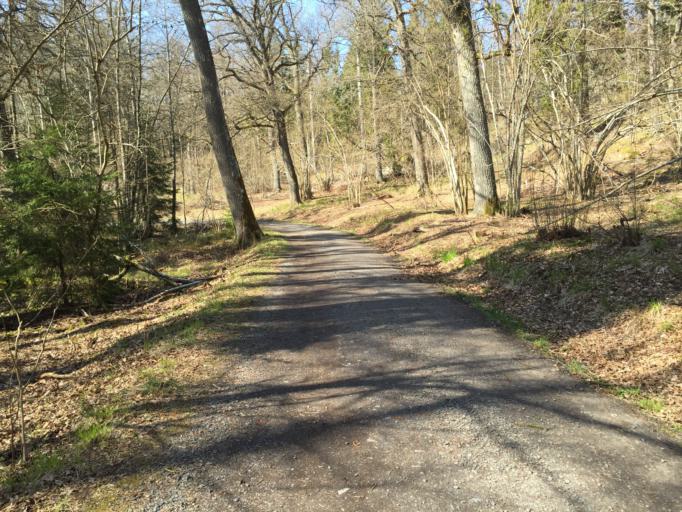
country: SE
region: Stockholm
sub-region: Nacka Kommun
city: Alta
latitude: 59.2704
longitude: 18.1660
